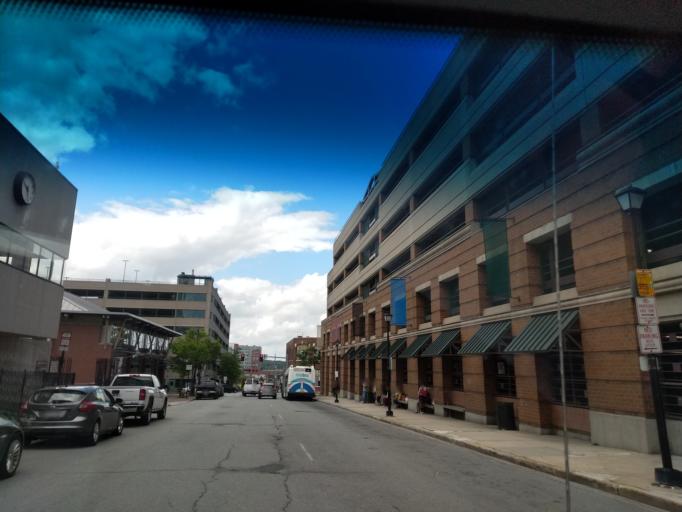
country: US
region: Maine
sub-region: Cumberland County
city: Portland
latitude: 43.6582
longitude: -70.2594
